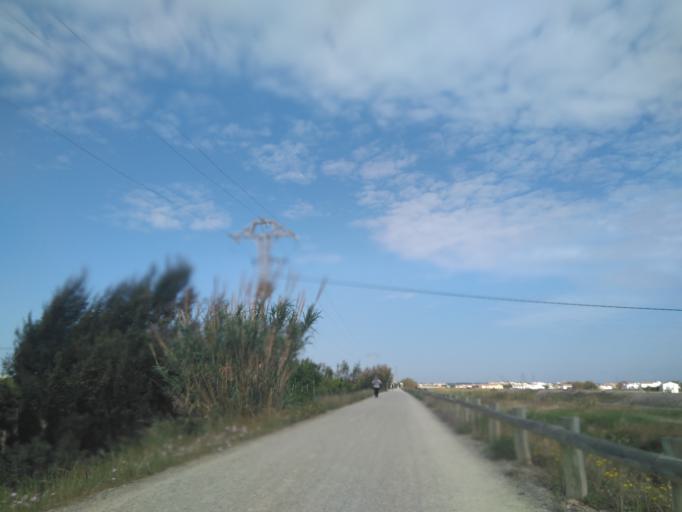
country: ES
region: Valencia
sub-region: Provincia de Valencia
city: Alboraya
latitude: 39.5026
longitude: -0.3336
